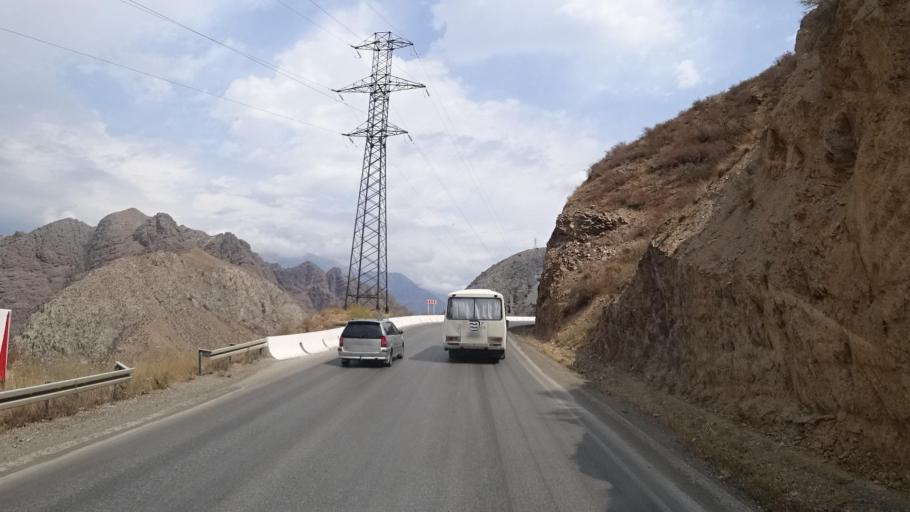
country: KG
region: Jalal-Abad
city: Tash-Kumyr
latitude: 41.5730
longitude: 72.5329
